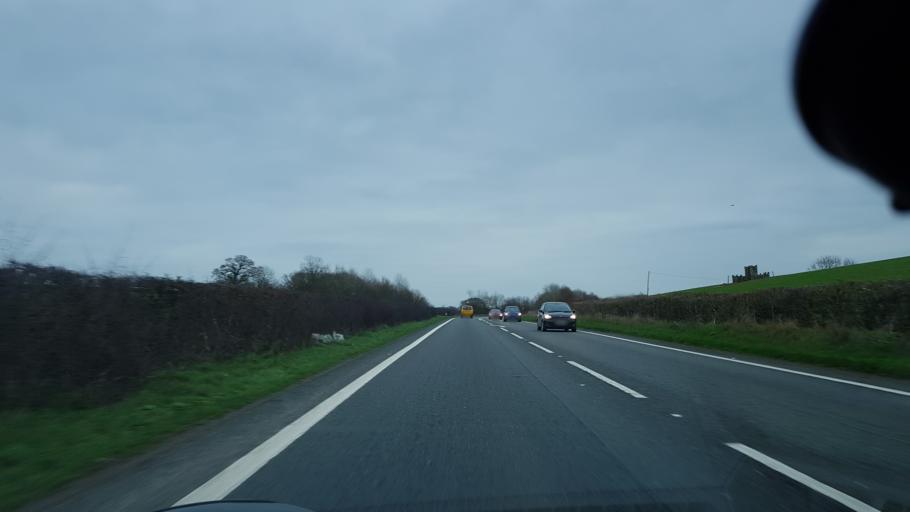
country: GB
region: England
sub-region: Somerset
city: Ilminster
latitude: 50.9540
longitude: -2.9639
